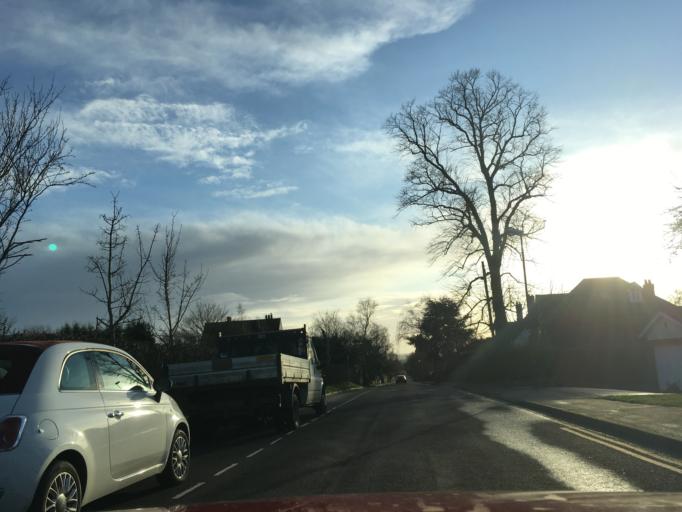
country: GB
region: England
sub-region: Warwickshire
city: Stratford-upon-Avon
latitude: 52.2029
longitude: -1.7023
